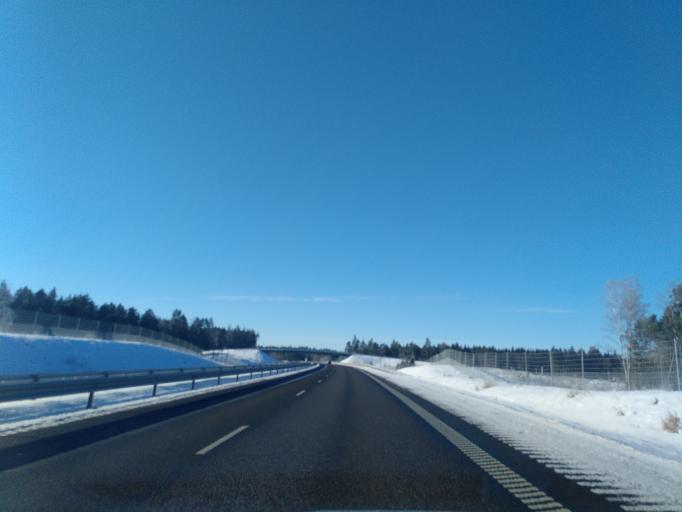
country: SE
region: Vaestra Goetaland
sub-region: Vargarda Kommun
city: Jonstorp
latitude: 57.9935
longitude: 12.7323
